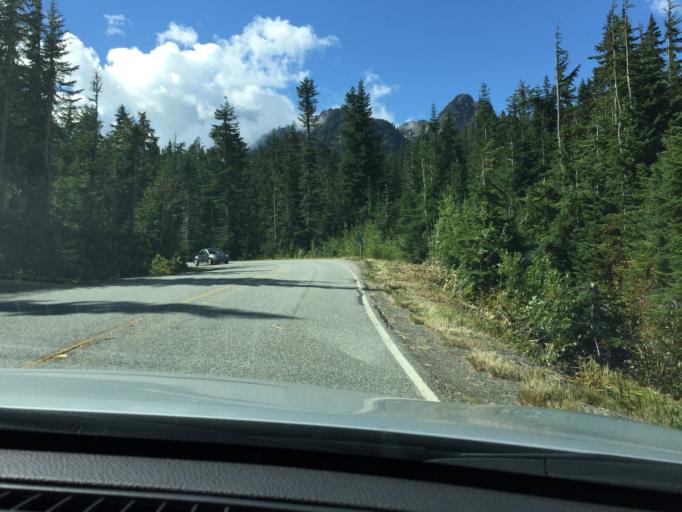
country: CA
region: British Columbia
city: Agassiz
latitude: 48.8647
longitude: -121.6679
